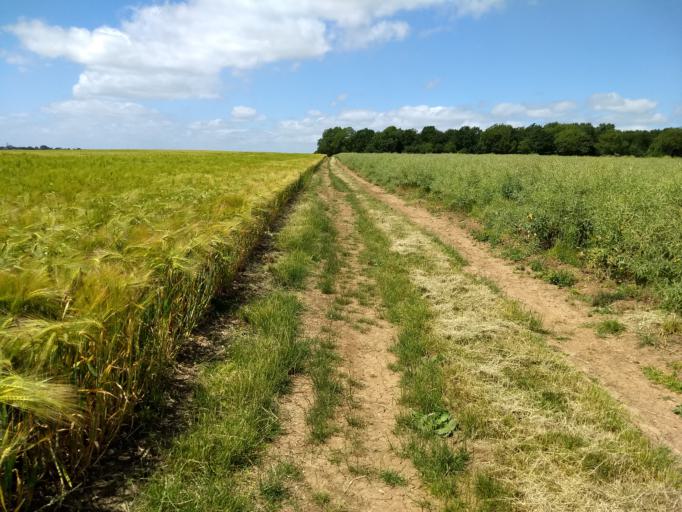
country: GB
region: England
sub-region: Milton Keynes
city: Calverton
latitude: 52.0182
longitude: -0.8544
